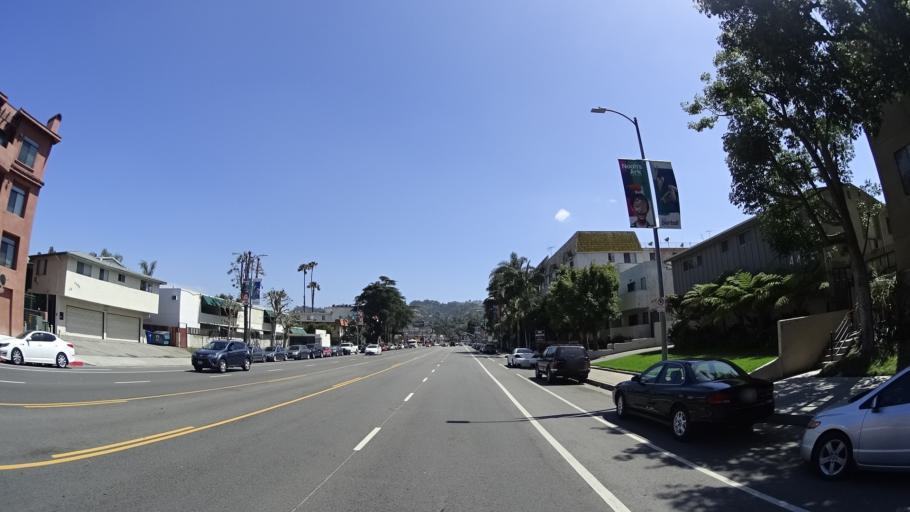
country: US
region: California
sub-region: Los Angeles County
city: Sherman Oaks
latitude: 34.1522
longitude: -118.4314
